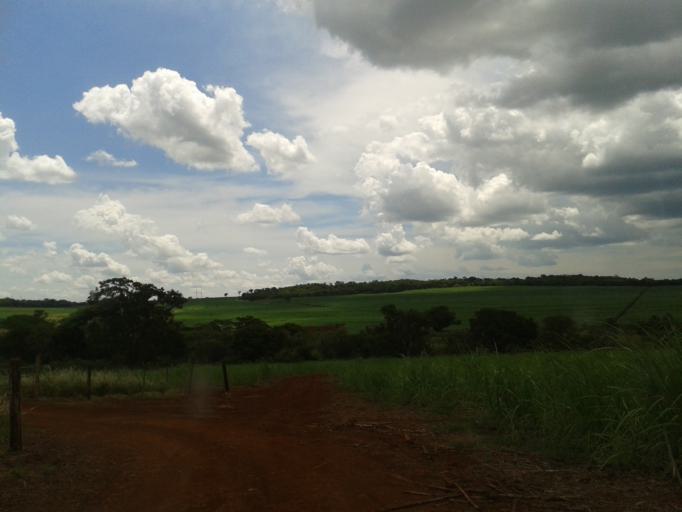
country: BR
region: Minas Gerais
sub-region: Centralina
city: Centralina
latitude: -18.6819
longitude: -49.2338
